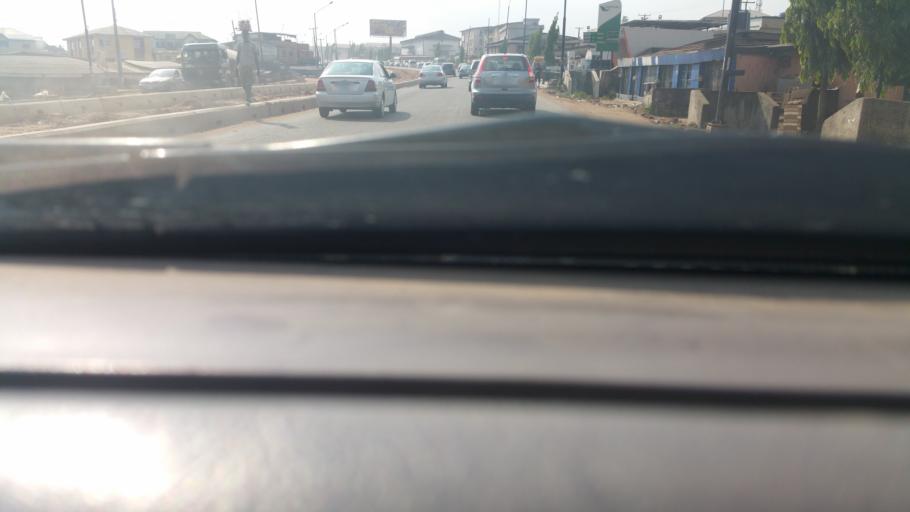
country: NG
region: Lagos
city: Agege
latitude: 6.6083
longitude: 3.3228
